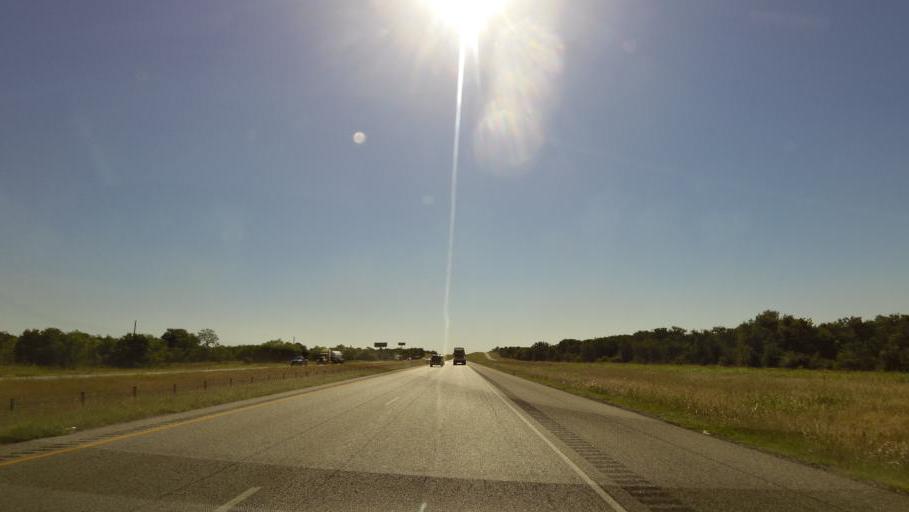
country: US
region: Texas
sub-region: Caldwell County
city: Luling
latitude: 29.6514
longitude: -97.5251
